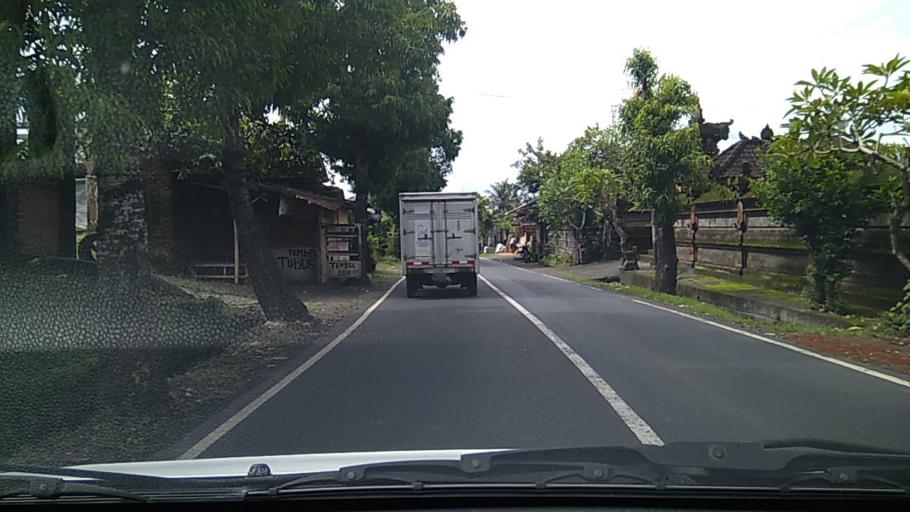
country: ID
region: Bali
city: Banjar Desa
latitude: -8.5851
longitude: 115.2543
